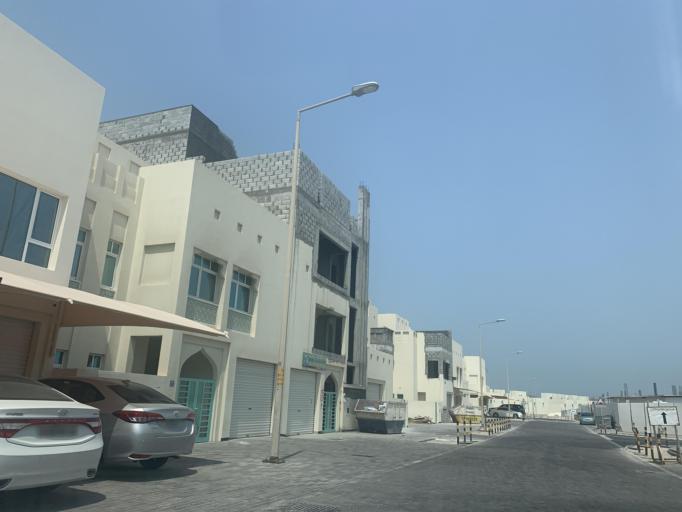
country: BH
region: Muharraq
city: Al Hadd
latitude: 26.2408
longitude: 50.6650
